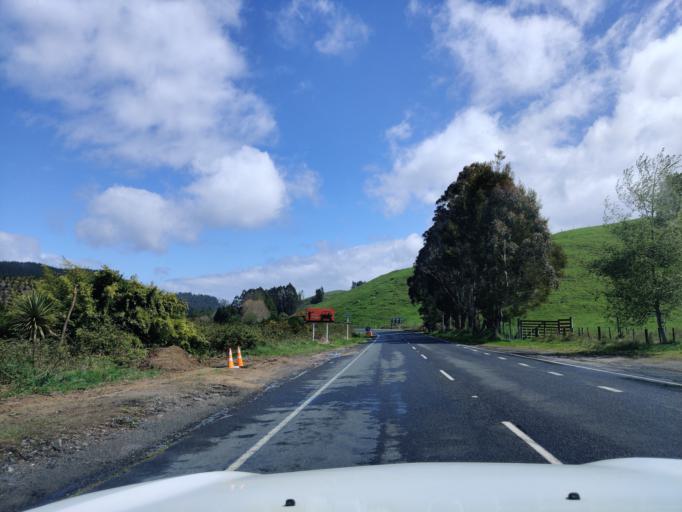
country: NZ
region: Bay of Plenty
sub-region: Rotorua District
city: Rotorua
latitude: -38.1684
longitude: 176.3201
